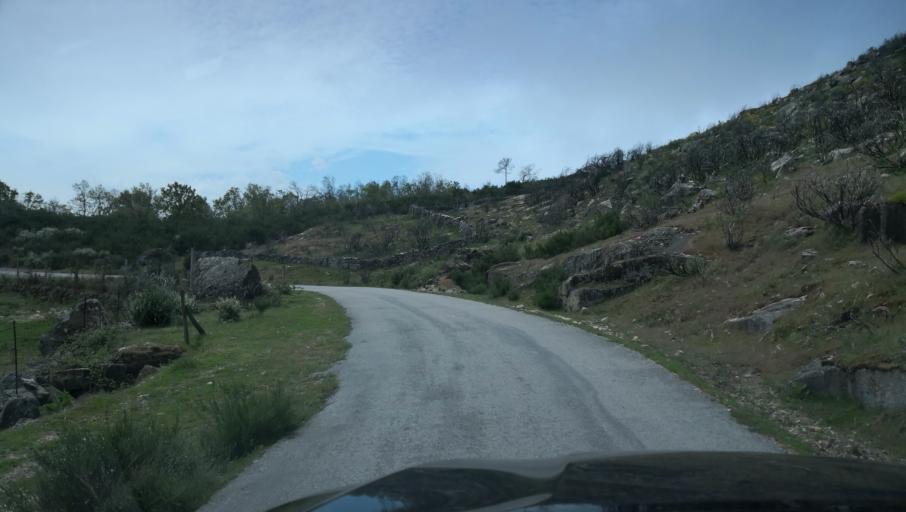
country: PT
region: Vila Real
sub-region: Vila Real
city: Vila Real
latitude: 41.2954
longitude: -7.8150
